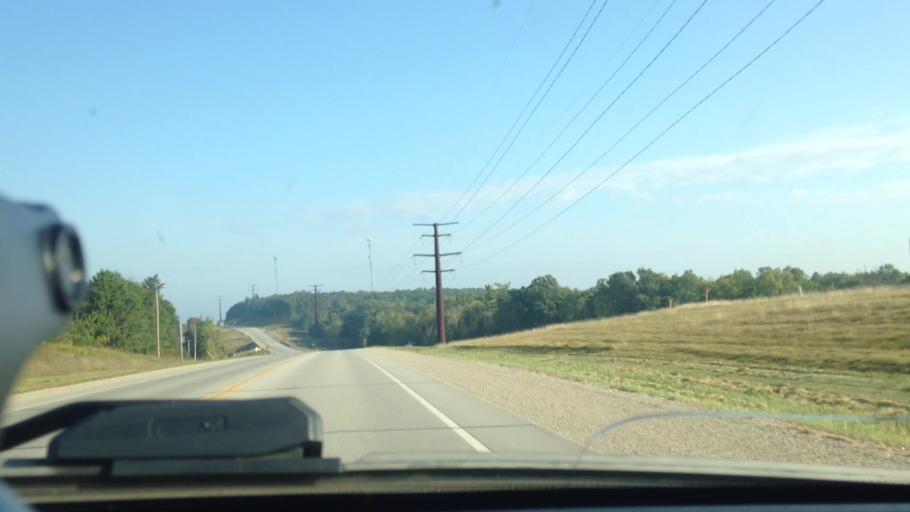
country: US
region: Wisconsin
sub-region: Marinette County
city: Peshtigo
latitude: 45.2045
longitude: -87.9943
